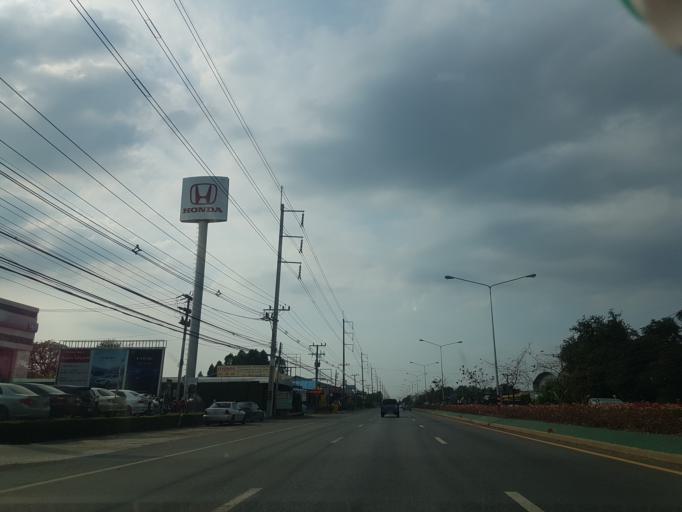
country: TH
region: Sara Buri
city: Phra Phutthabat
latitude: 14.7426
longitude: 100.7611
